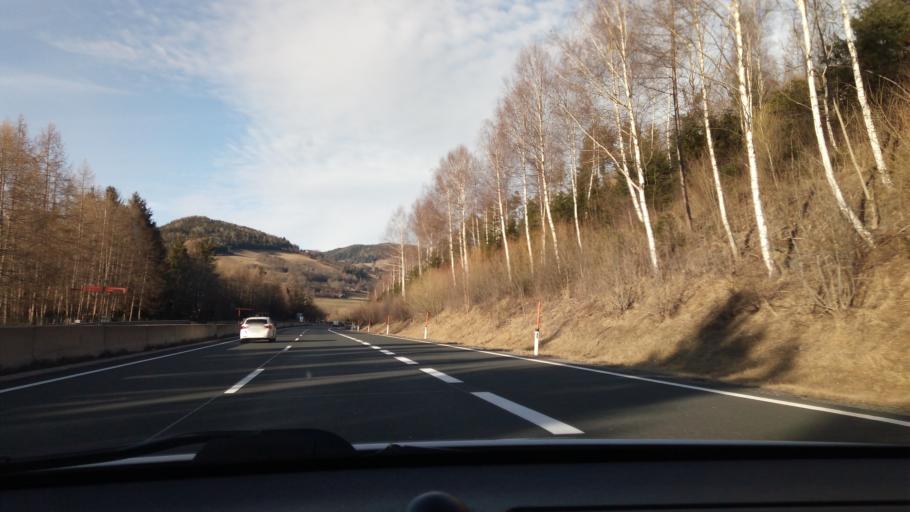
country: AT
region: Carinthia
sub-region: Politischer Bezirk Spittal an der Drau
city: Gmuend
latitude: 46.9027
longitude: 13.5423
